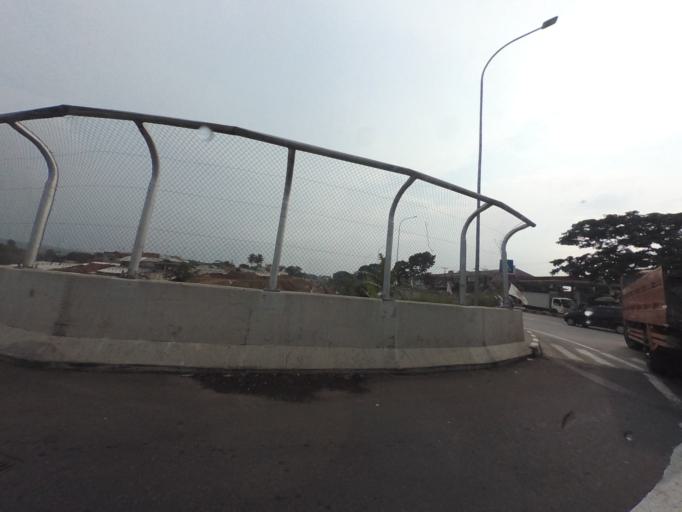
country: ID
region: West Java
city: Cicurug
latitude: -6.7518
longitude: 106.8000
